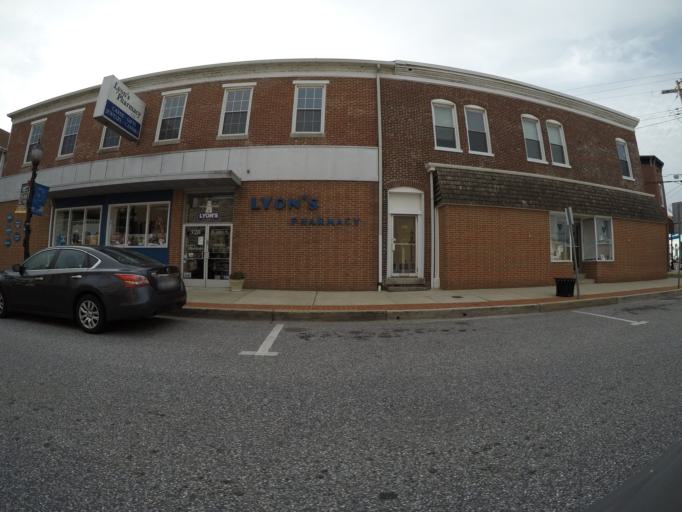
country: US
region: Maryland
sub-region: Harford County
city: Havre de Grace
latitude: 39.5506
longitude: -76.0905
